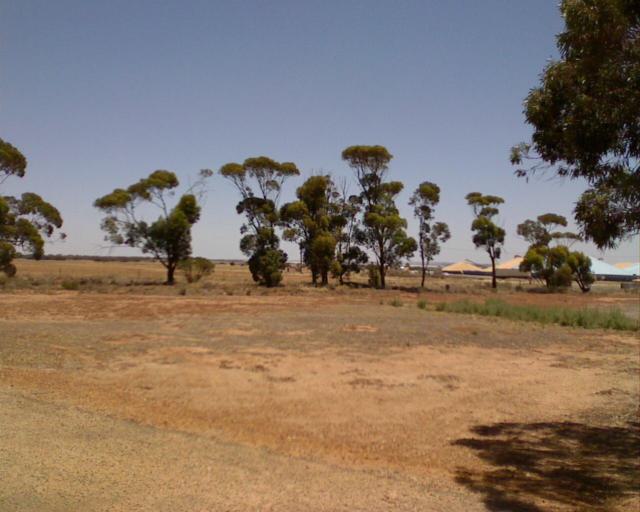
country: AU
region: Western Australia
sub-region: Wongan-Ballidu
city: Wongan Hills
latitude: -30.3600
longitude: 117.1136
